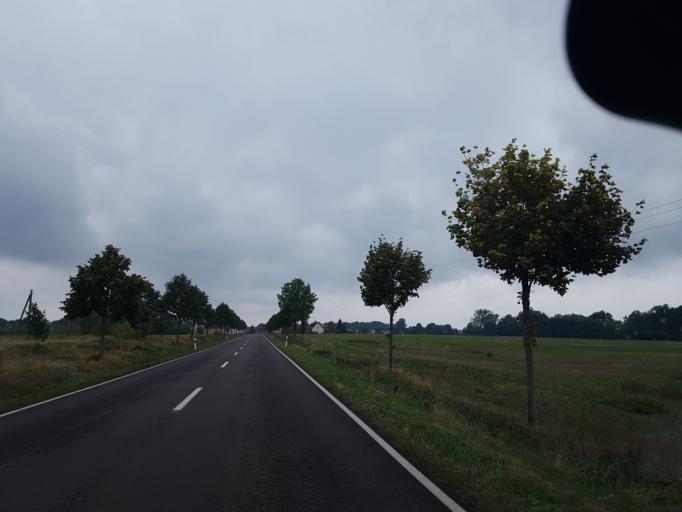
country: DE
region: Saxony-Anhalt
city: Tucheim
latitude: 52.3119
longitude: 12.1295
